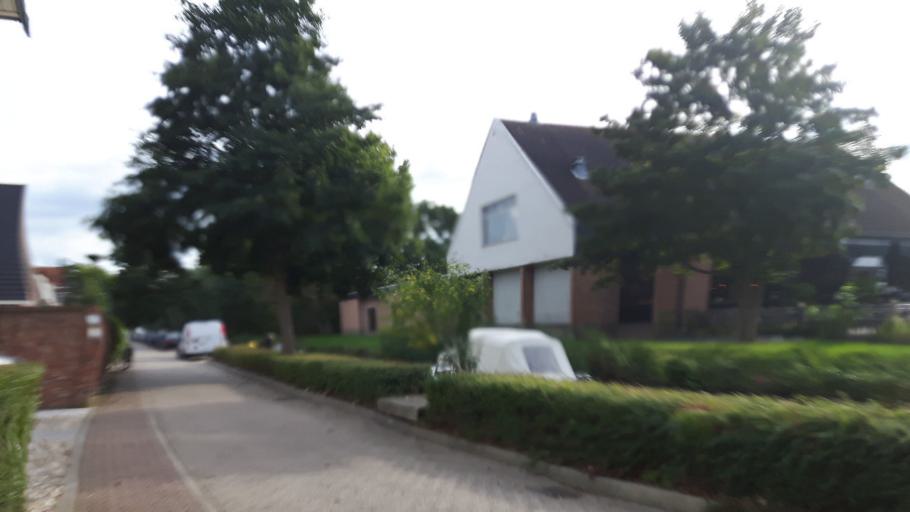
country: NL
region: Utrecht
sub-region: Gemeente Woerden
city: Woerden
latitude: 52.0839
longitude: 4.8925
